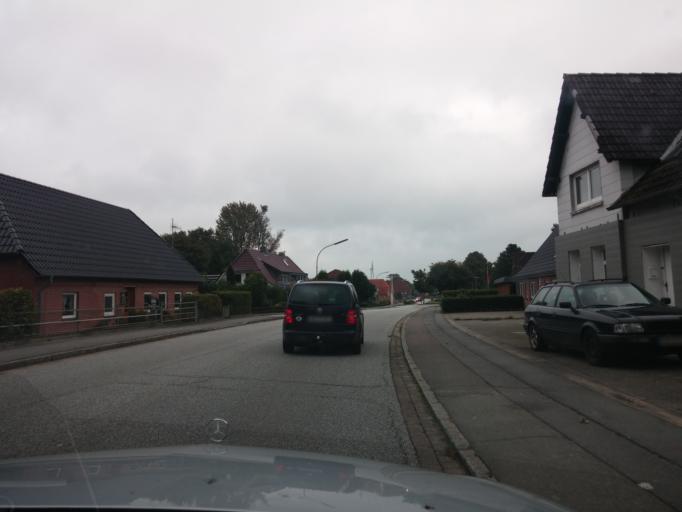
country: DE
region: Schleswig-Holstein
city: Silberstedt
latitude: 54.5180
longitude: 9.3659
